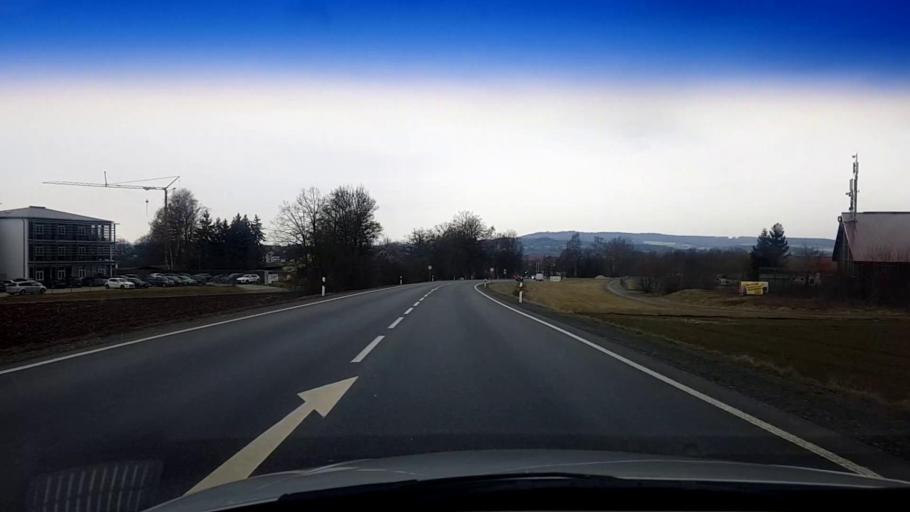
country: DE
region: Bavaria
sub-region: Upper Franconia
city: Kulmbach
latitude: 50.0870
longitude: 11.4575
